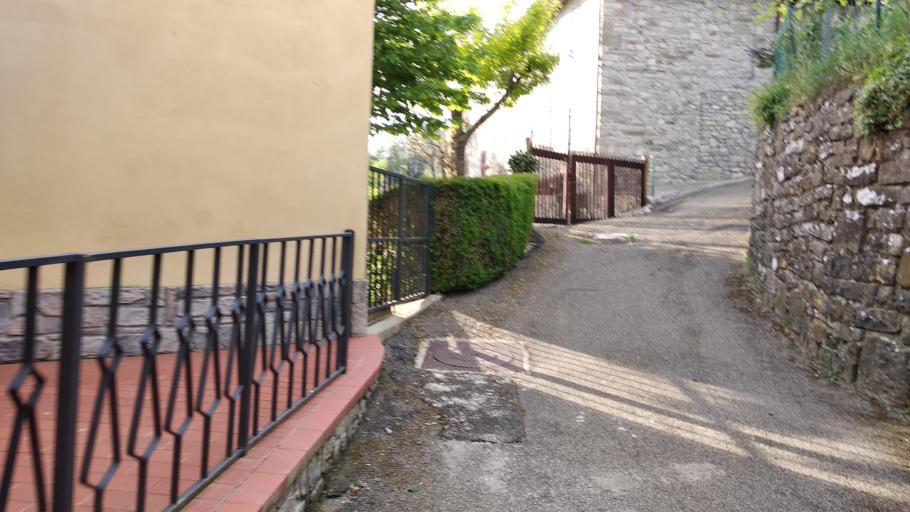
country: IT
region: Tuscany
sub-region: Province of Arezzo
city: Chiusi della Verna
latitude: 43.7499
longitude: 11.9339
